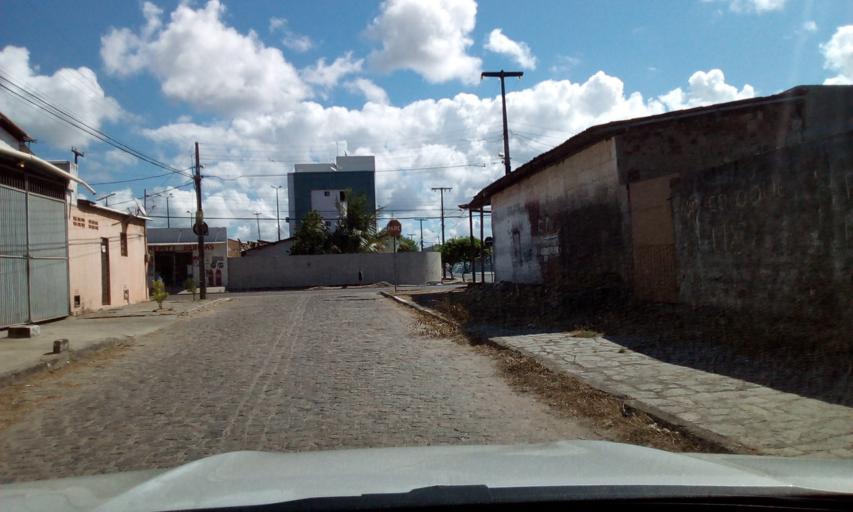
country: BR
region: Paraiba
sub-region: Joao Pessoa
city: Joao Pessoa
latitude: -7.1762
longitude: -34.8836
